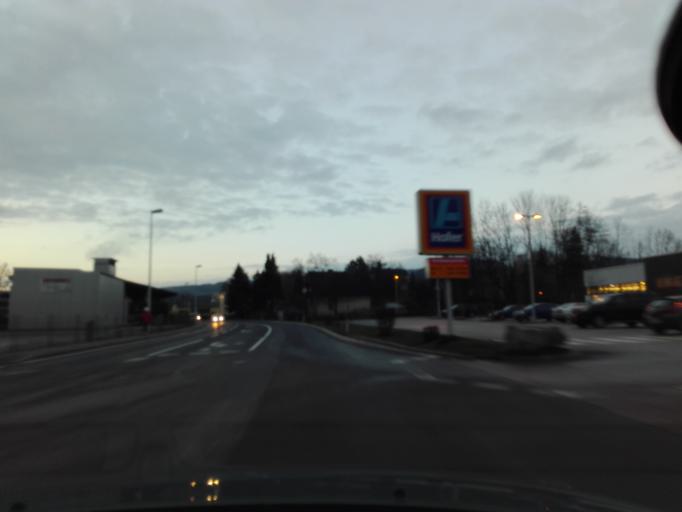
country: AT
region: Upper Austria
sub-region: Politischer Bezirk Perg
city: Bad Kreuzen
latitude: 48.2190
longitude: 14.8540
